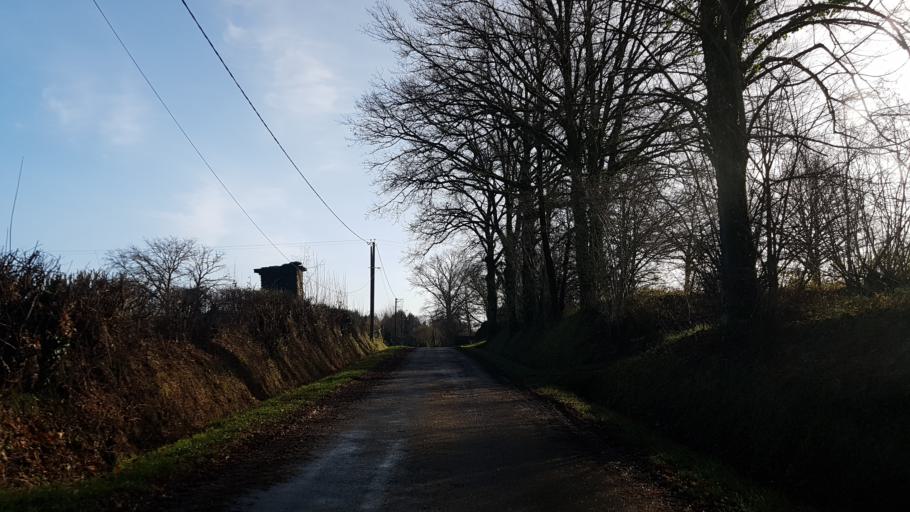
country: FR
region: Poitou-Charentes
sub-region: Departement de la Charente
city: Etagnac
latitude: 45.9205
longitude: 0.8216
